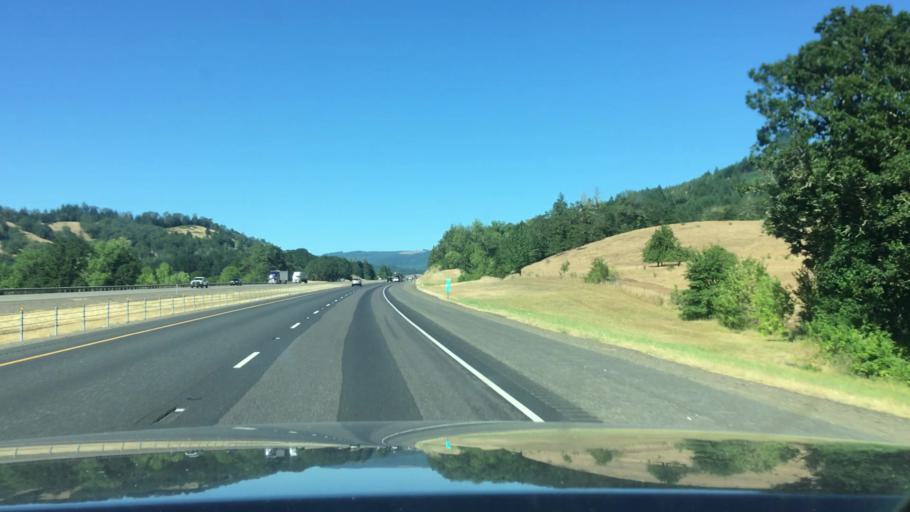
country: US
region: Oregon
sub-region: Douglas County
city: Yoncalla
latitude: 43.5922
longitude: -123.2475
